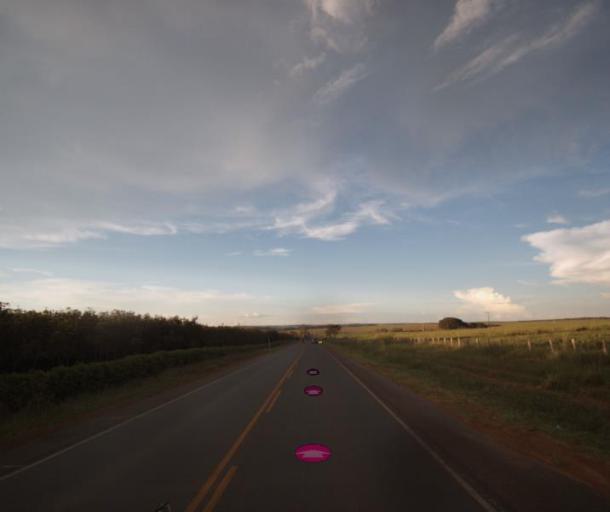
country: BR
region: Goias
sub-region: Anapolis
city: Anapolis
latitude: -16.1960
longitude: -48.9081
